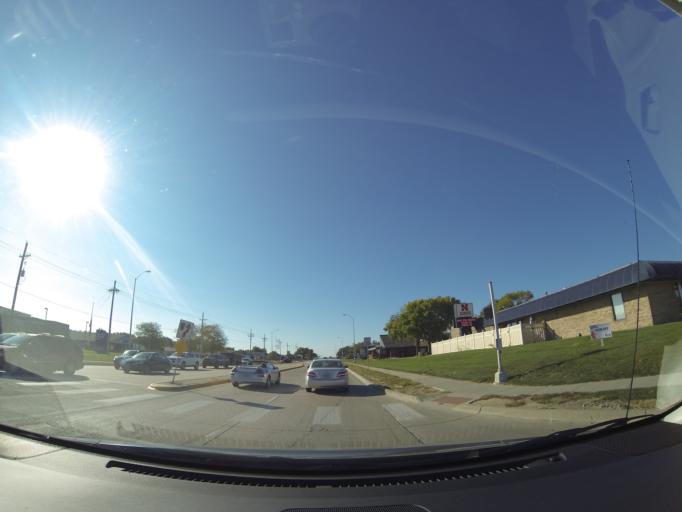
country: US
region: Nebraska
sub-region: Sarpy County
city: Gretna
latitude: 41.1468
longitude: -96.2391
